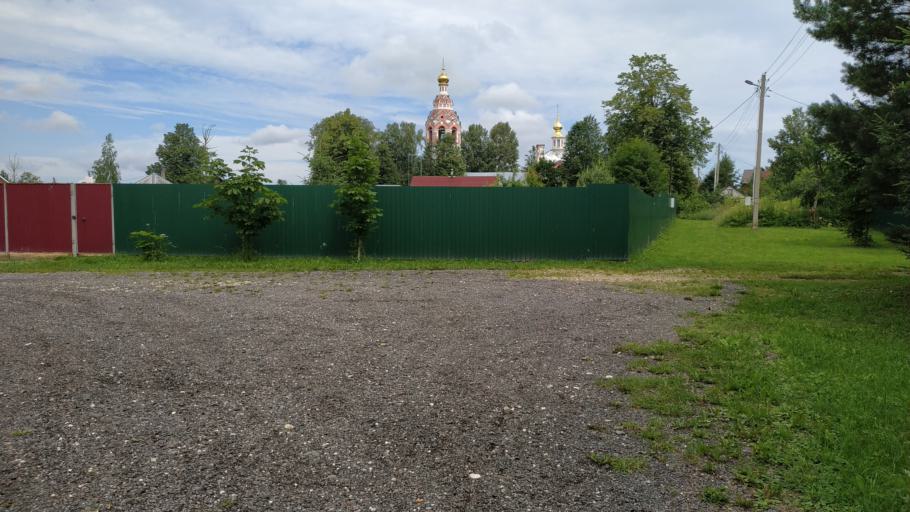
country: RU
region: Moskovskaya
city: Dorokhovo
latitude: 55.5573
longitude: 36.3171
